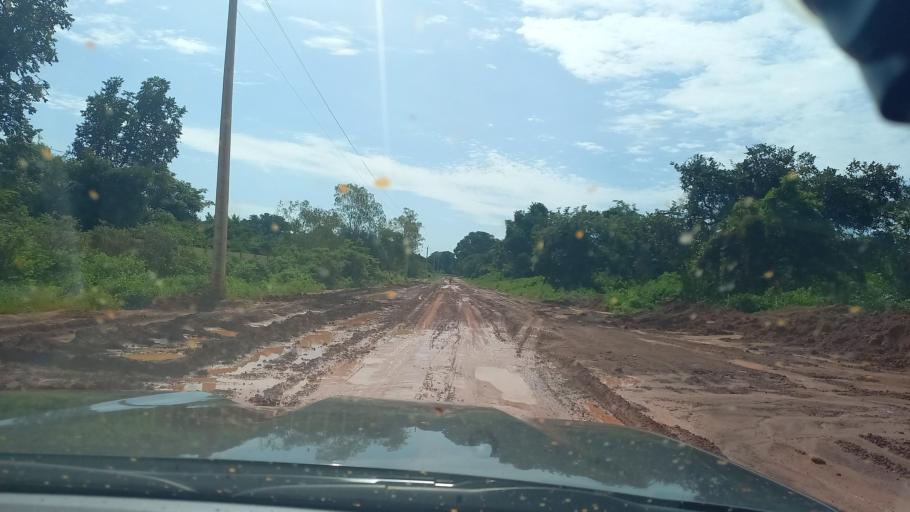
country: SN
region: Ziguinchor
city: Ziguinchor
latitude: 12.6702
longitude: -16.1883
